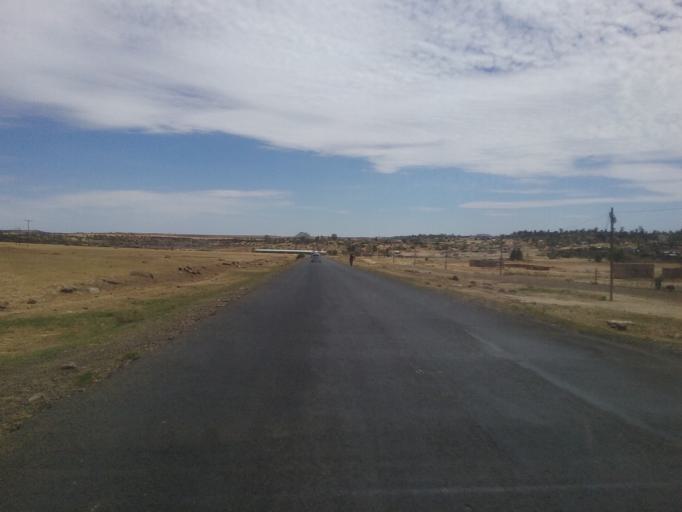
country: LS
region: Mafeteng
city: Mafeteng
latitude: -29.8523
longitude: 27.2314
